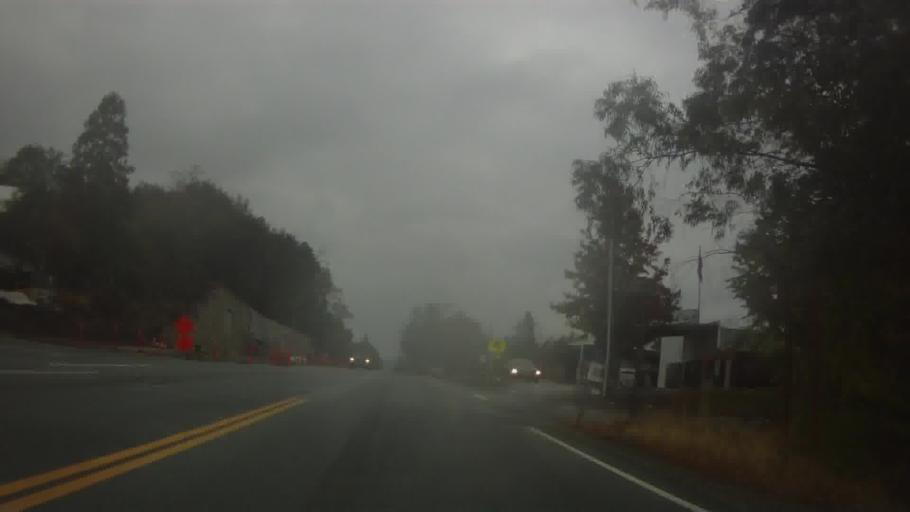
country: US
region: California
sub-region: Shasta County
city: Shasta
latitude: 40.5963
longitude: -122.4880
